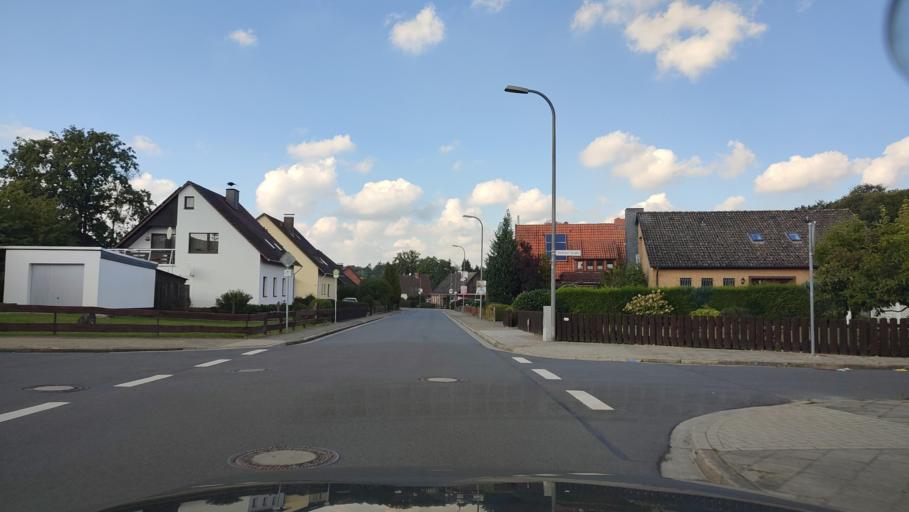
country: DE
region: Lower Saxony
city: Bomlitz
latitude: 52.9019
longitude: 9.6645
